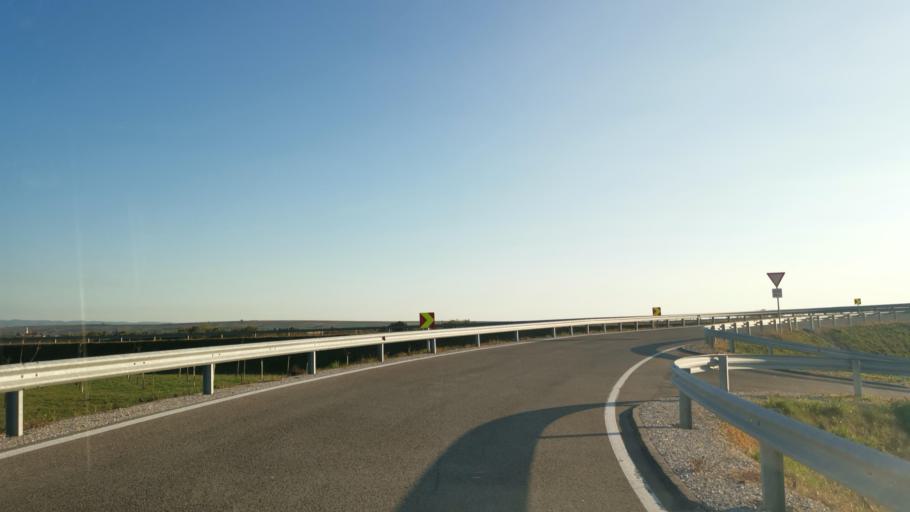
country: HU
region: Heves
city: Maklar
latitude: 47.7962
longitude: 20.3935
